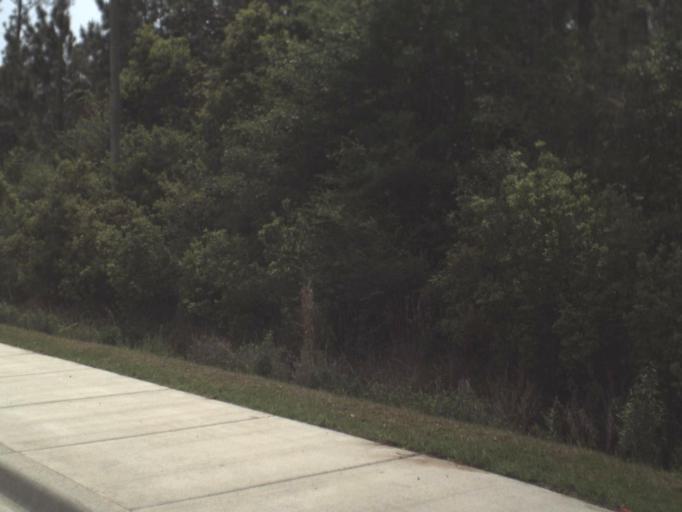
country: US
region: Florida
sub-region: Santa Rosa County
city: Bagdad
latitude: 30.5590
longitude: -87.0872
